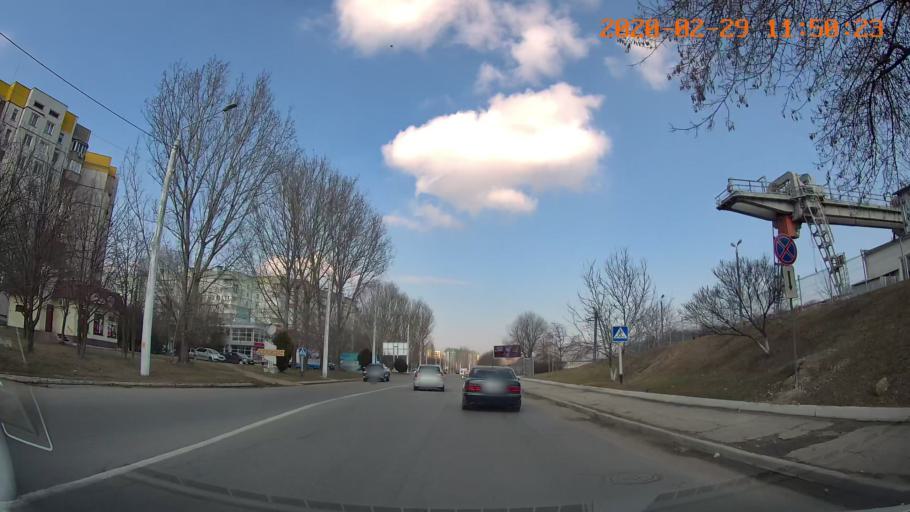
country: MD
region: Telenesti
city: Ribnita
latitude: 47.7576
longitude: 28.9909
